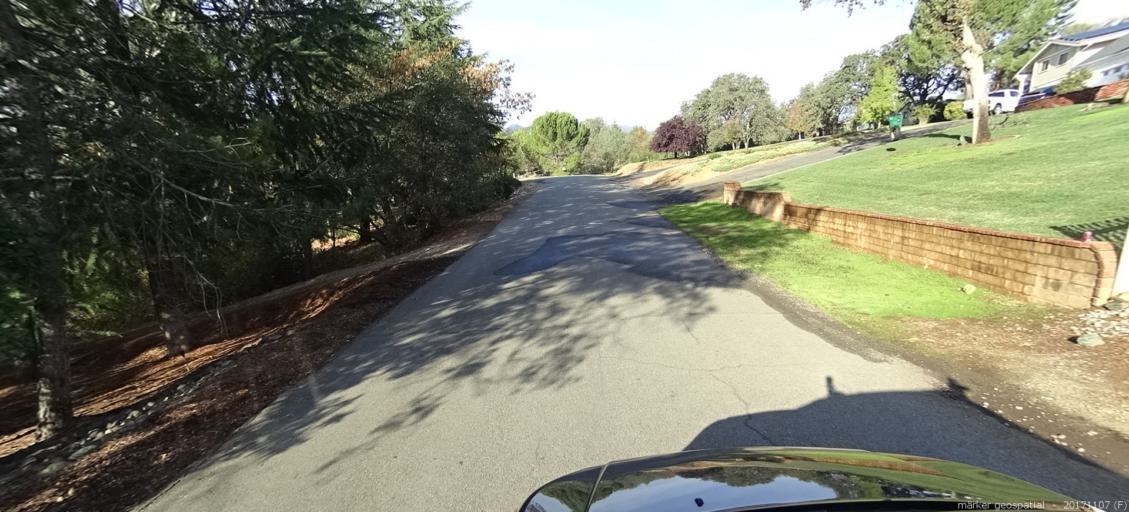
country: US
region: California
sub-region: Shasta County
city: Shasta
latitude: 40.5420
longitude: -122.4607
